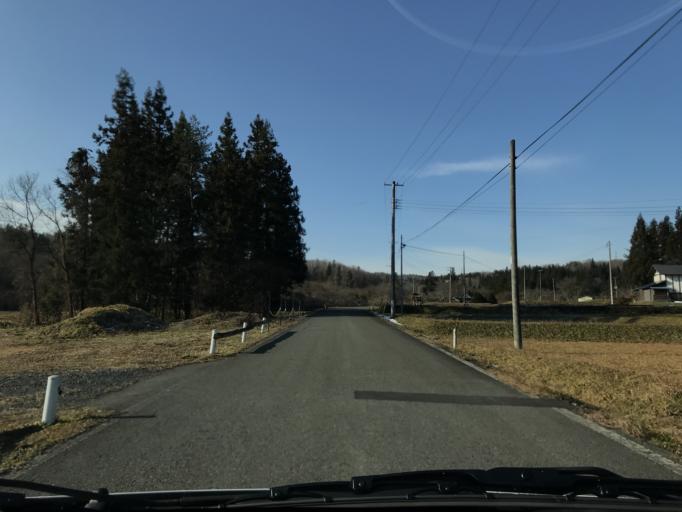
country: JP
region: Iwate
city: Ichinoseki
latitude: 38.9674
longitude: 141.0514
